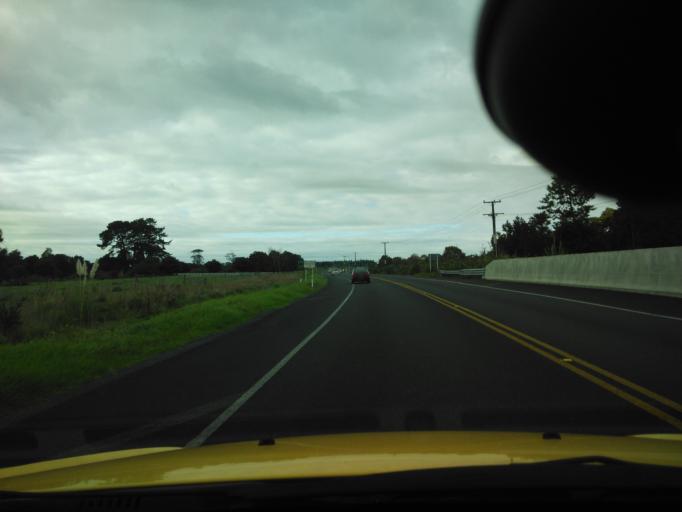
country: NZ
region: Waikato
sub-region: Waikato District
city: Ngaruawahia
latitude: -37.6162
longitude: 175.1970
